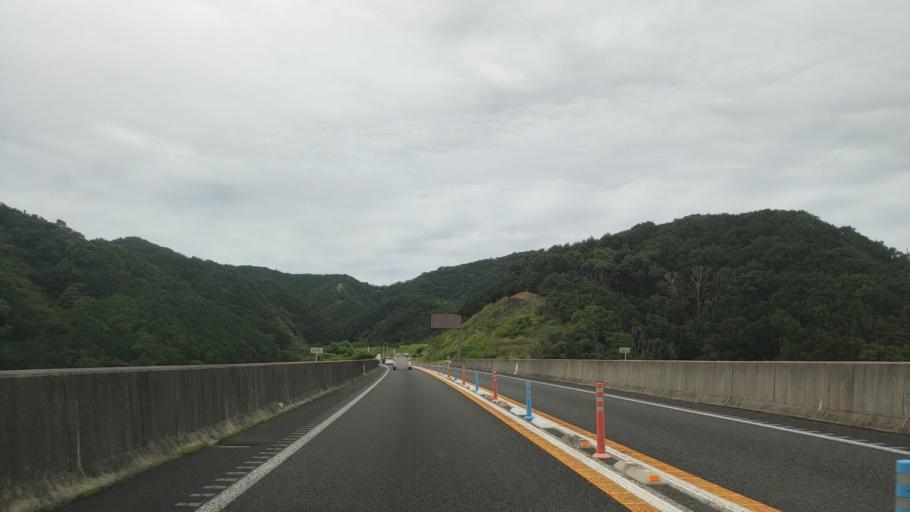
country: JP
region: Wakayama
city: Tanabe
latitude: 33.8014
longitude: 135.2747
